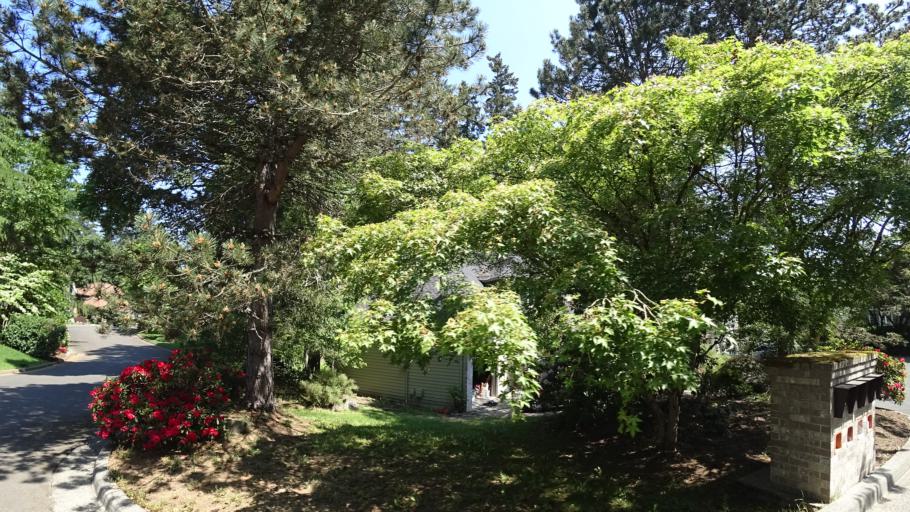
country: US
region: Oregon
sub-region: Clackamas County
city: Lake Oswego
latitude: 45.4407
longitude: -122.7110
